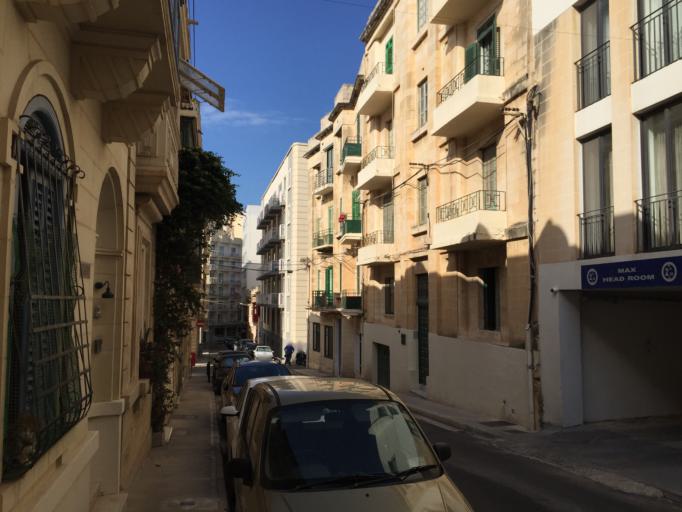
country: MT
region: Tas-Sliema
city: Sliema
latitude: 35.9131
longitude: 14.5052
